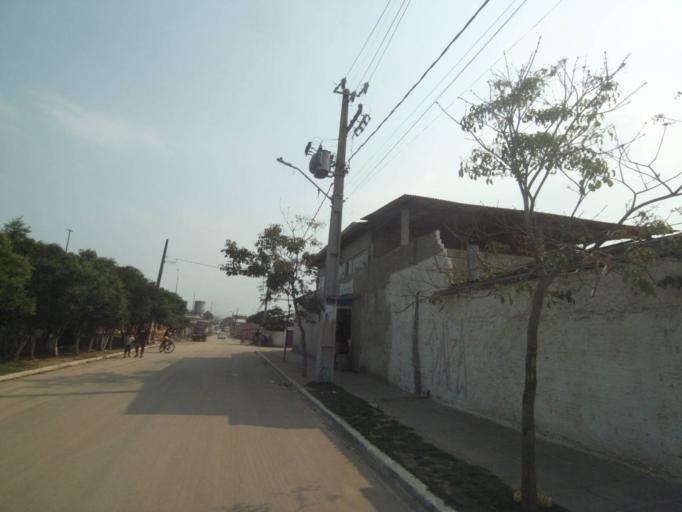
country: BR
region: Parana
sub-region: Sao Jose Dos Pinhais
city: Sao Jose dos Pinhais
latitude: -25.5305
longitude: -49.2310
